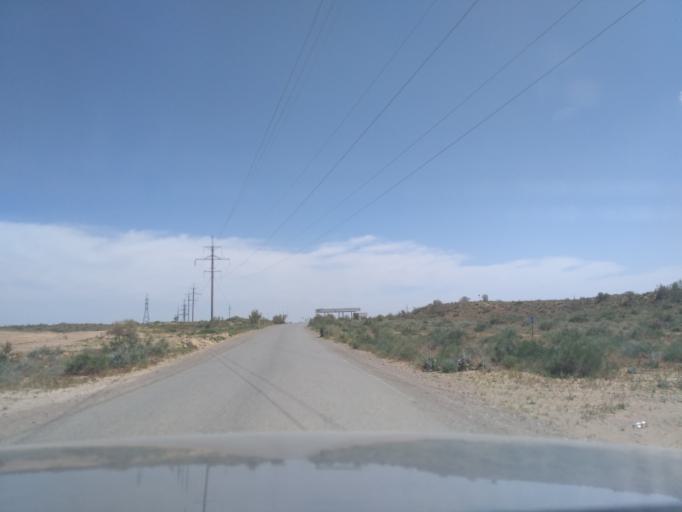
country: KZ
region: Ongtustik Qazaqstan
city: Sholaqqkorghan
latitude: 44.2346
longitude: 68.9303
